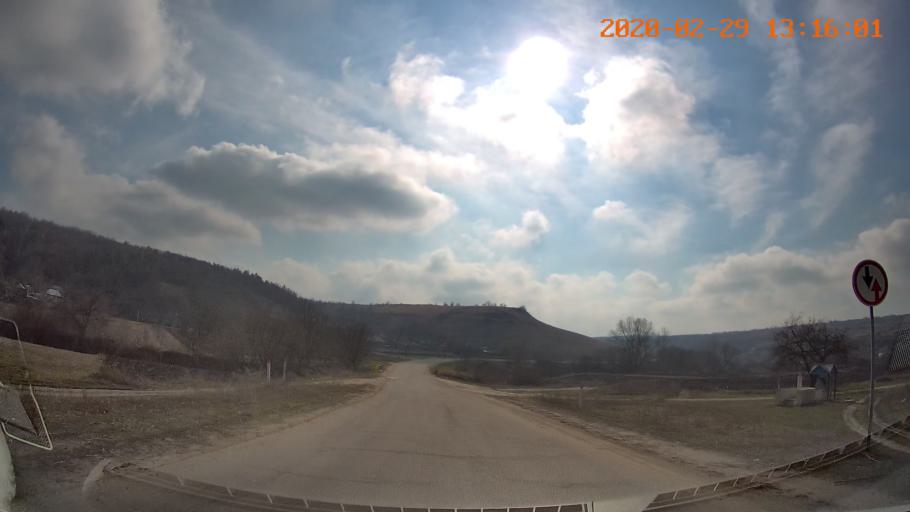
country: MD
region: Telenesti
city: Camenca
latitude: 48.0059
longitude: 28.6666
